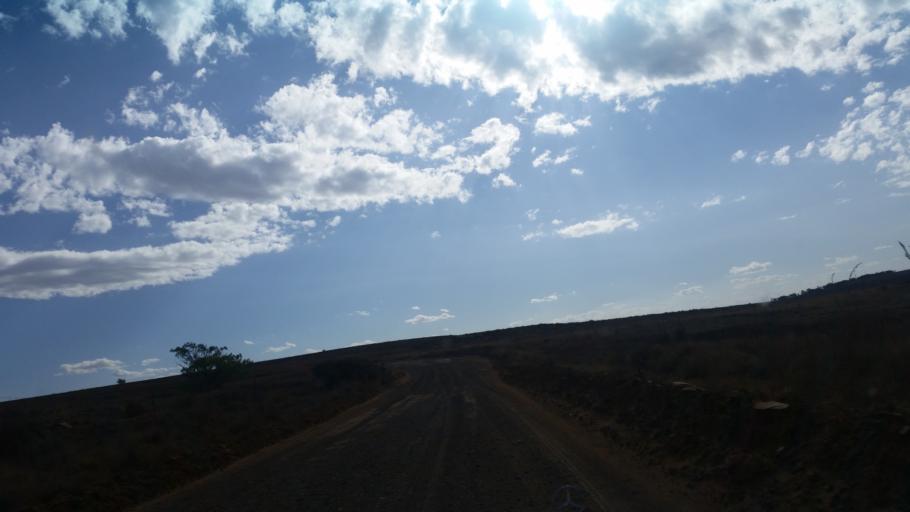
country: ZA
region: Orange Free State
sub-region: Thabo Mofutsanyana District Municipality
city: Phuthaditjhaba
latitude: -28.3506
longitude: 28.6073
